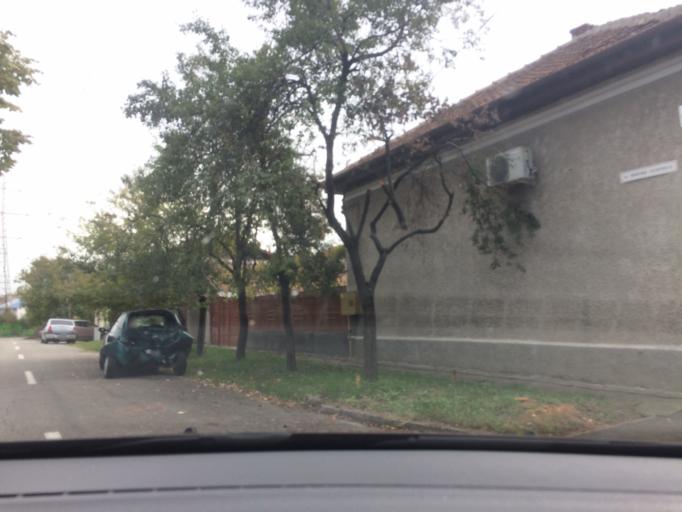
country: RO
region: Timis
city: Timisoara
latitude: 45.7542
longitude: 21.2052
